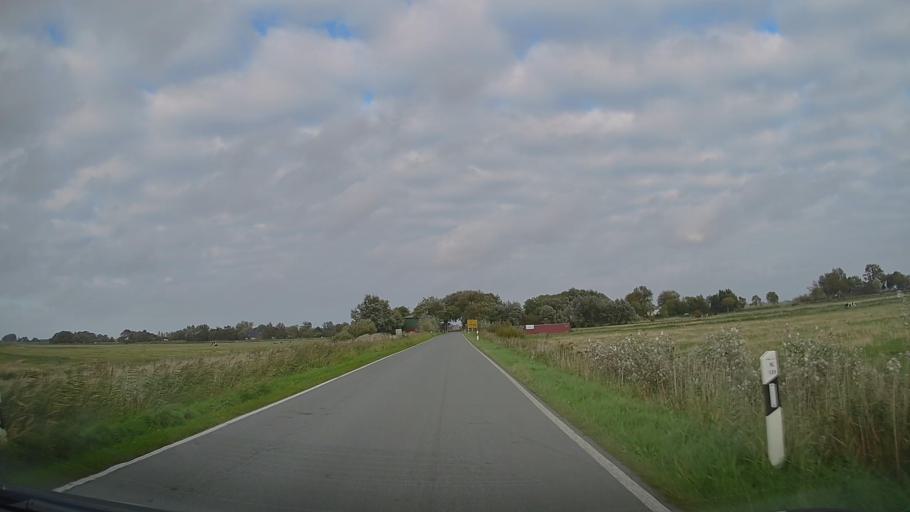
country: DE
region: Schleswig-Holstein
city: Osterhever
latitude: 54.3795
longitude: 8.7545
